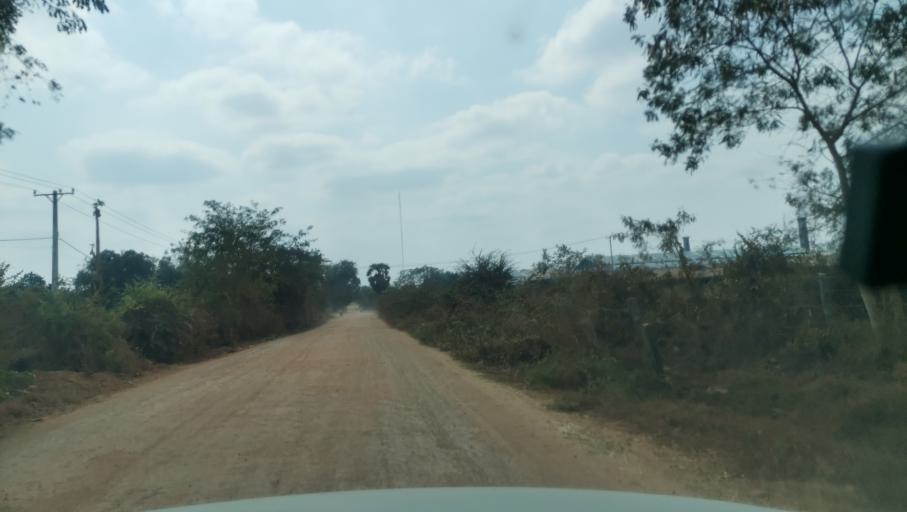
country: KH
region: Battambang
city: Battambang
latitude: 13.0667
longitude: 103.1693
